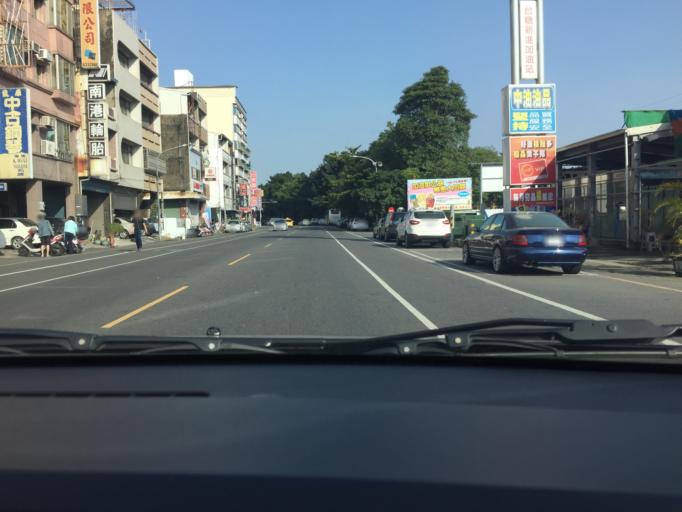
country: TW
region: Taiwan
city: Xinying
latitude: 23.3018
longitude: 120.3172
